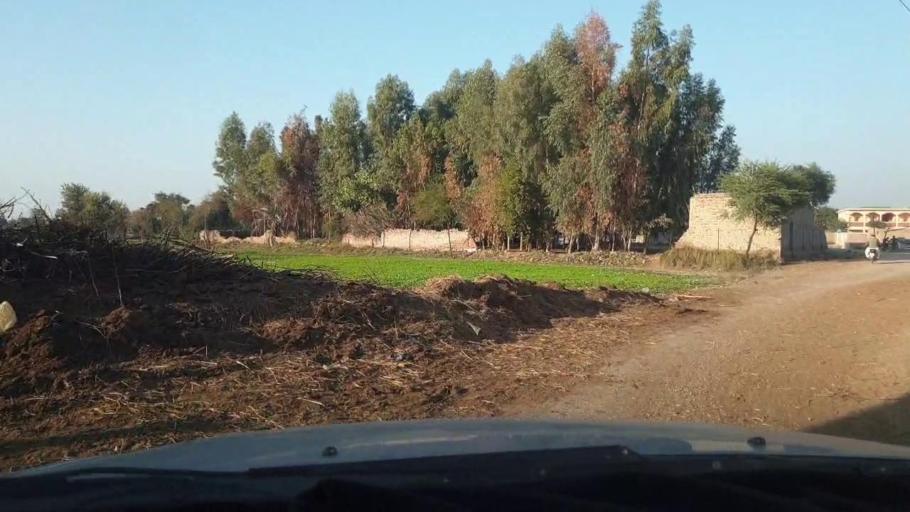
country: PK
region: Sindh
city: Mirpur Mathelo
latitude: 27.9989
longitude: 69.5151
